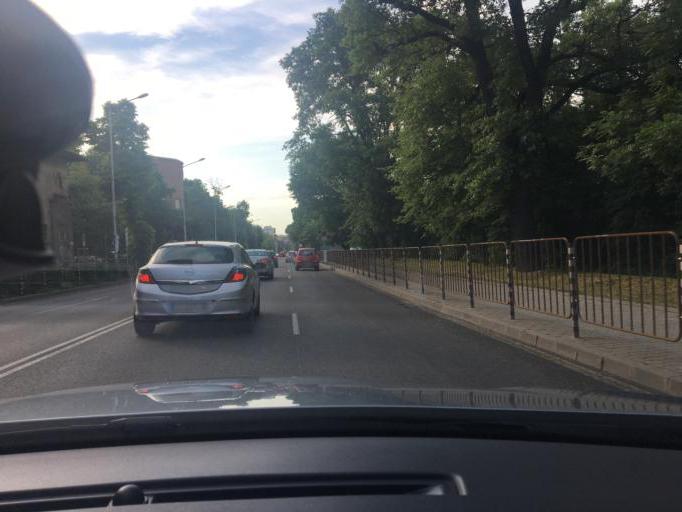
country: BG
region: Sofia-Capital
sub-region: Stolichna Obshtina
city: Sofia
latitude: 42.6829
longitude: 23.3353
